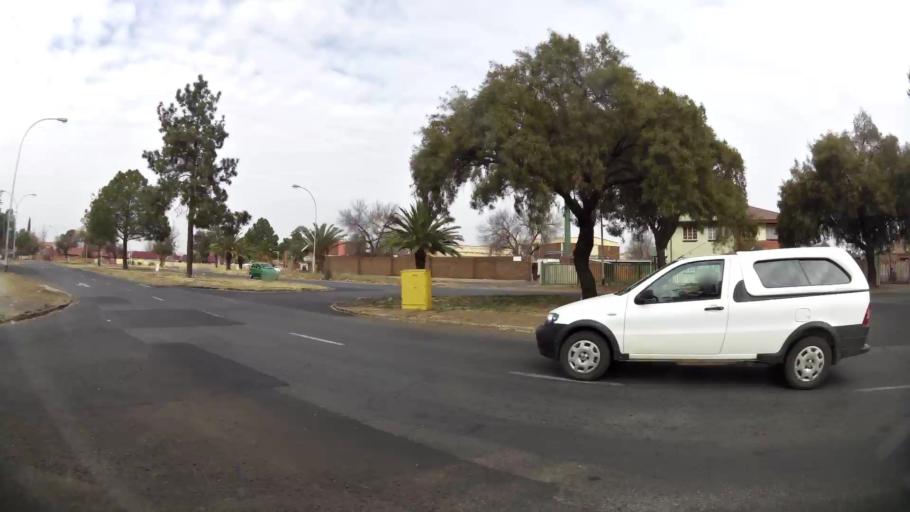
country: ZA
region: Orange Free State
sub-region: Mangaung Metropolitan Municipality
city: Bloemfontein
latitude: -29.1288
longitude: 26.1916
